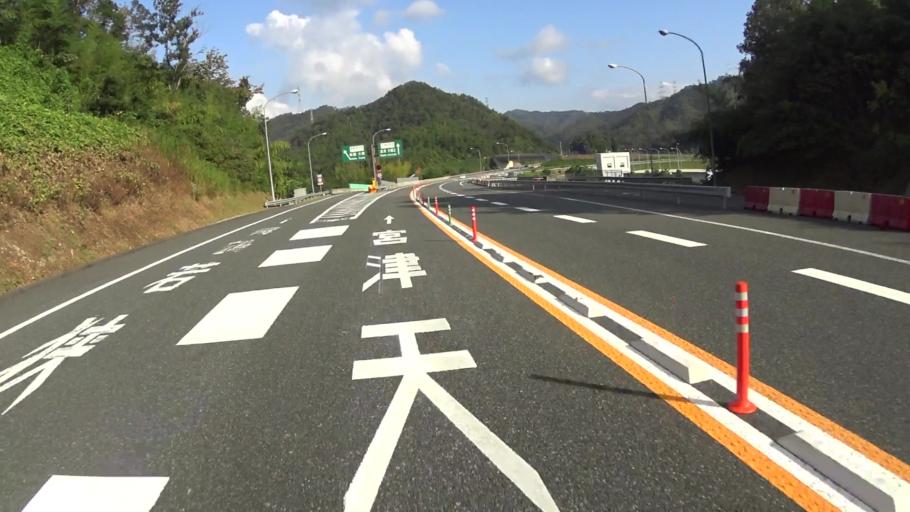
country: JP
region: Kyoto
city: Ayabe
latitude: 35.3519
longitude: 135.2899
